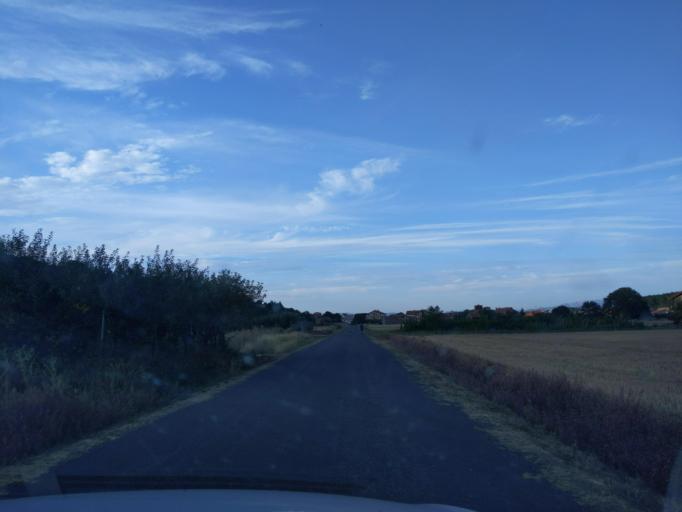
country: ES
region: La Rioja
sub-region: Provincia de La Rioja
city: Santurdejo
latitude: 42.3849
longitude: -2.9830
